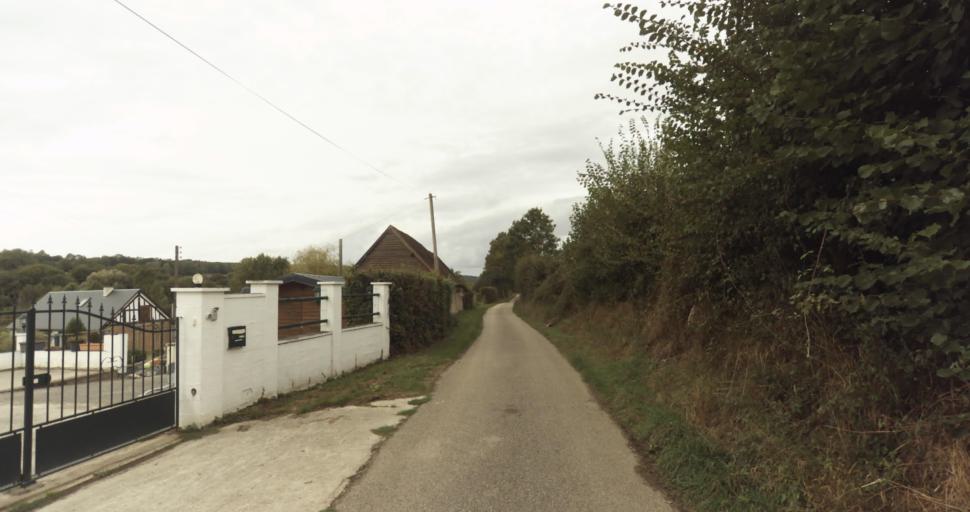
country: FR
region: Lower Normandy
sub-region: Departement de l'Orne
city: Gace
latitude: 48.8208
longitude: 0.2851
